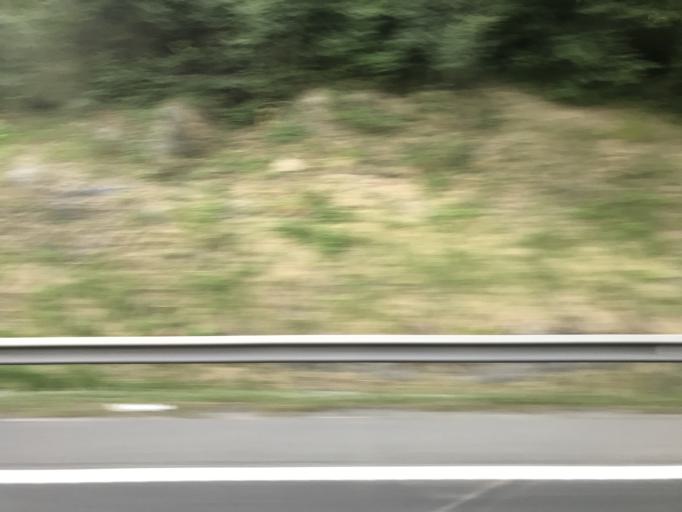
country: ES
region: Basque Country
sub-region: Provincia de Guipuzcoa
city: Arama
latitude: 43.0644
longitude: -2.1659
